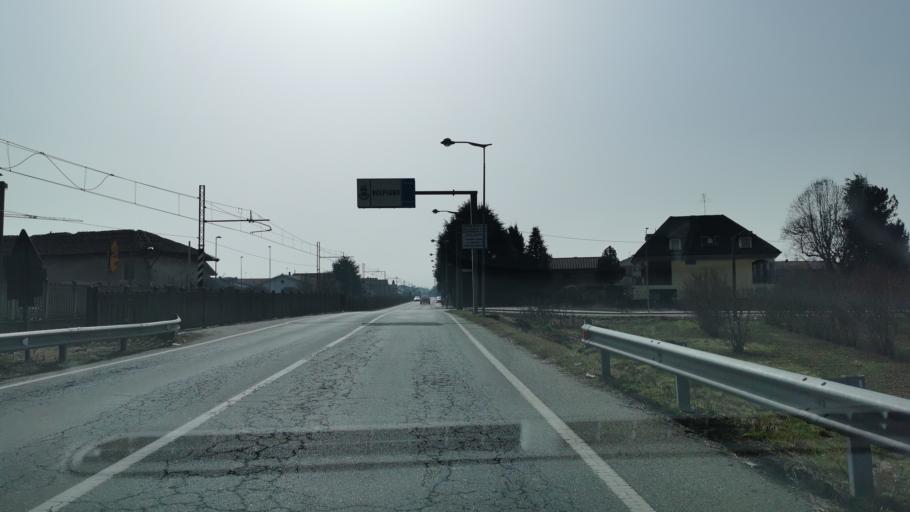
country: IT
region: Piedmont
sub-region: Provincia di Torino
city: Volpiano
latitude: 45.2092
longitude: 7.7805
